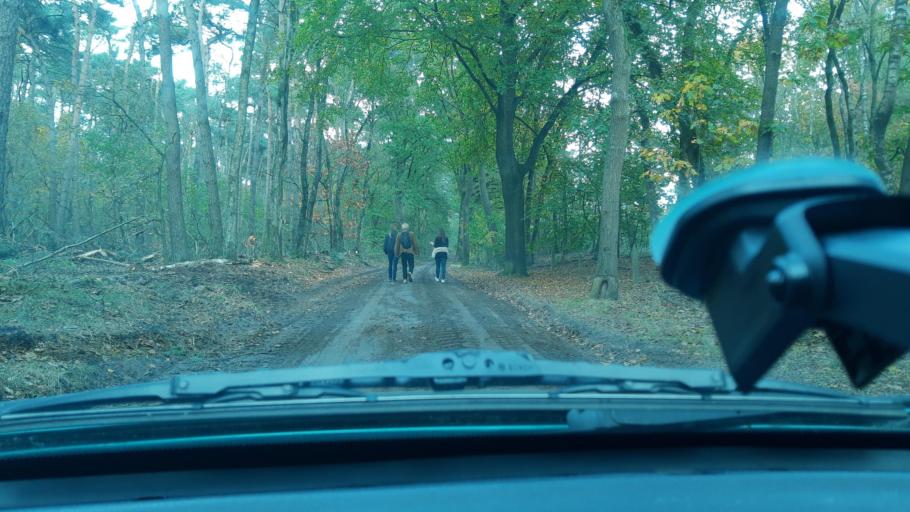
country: NL
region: Limburg
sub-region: Gemeente Gennep
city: Gennep
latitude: 51.6575
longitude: 6.0089
